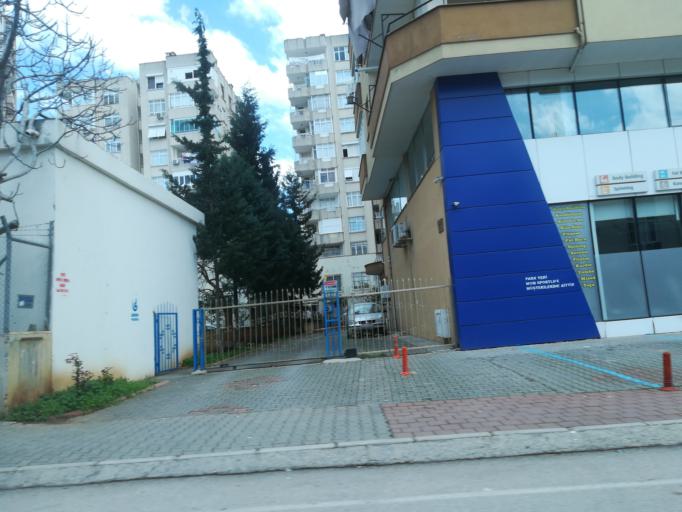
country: TR
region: Adana
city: Adana
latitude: 37.0342
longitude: 35.3127
